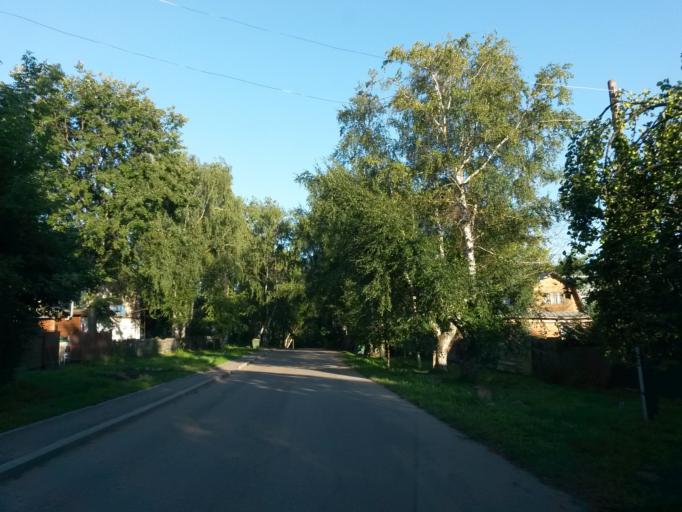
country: RU
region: Jaroslavl
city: Tutayev
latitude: 57.8810
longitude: 39.5433
